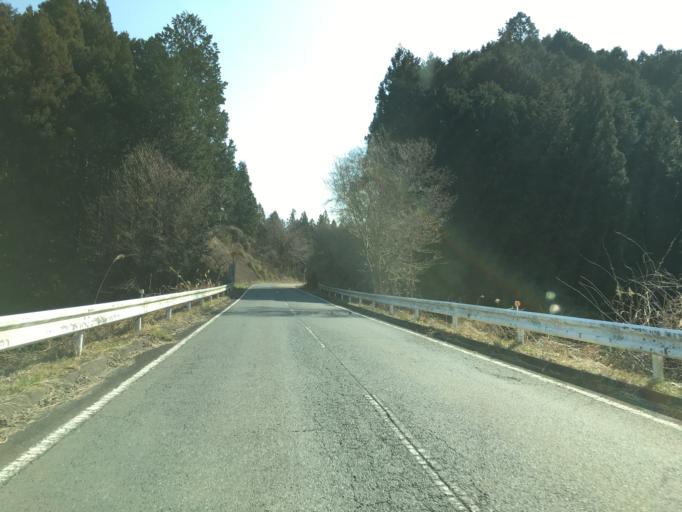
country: JP
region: Ibaraki
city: Daigo
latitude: 36.7879
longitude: 140.4702
